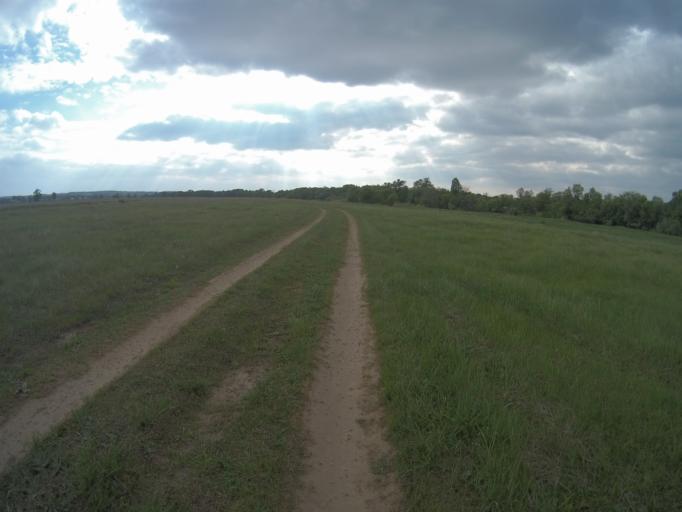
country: RU
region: Vladimir
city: Raduzhnyy
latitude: 56.0322
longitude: 40.2281
